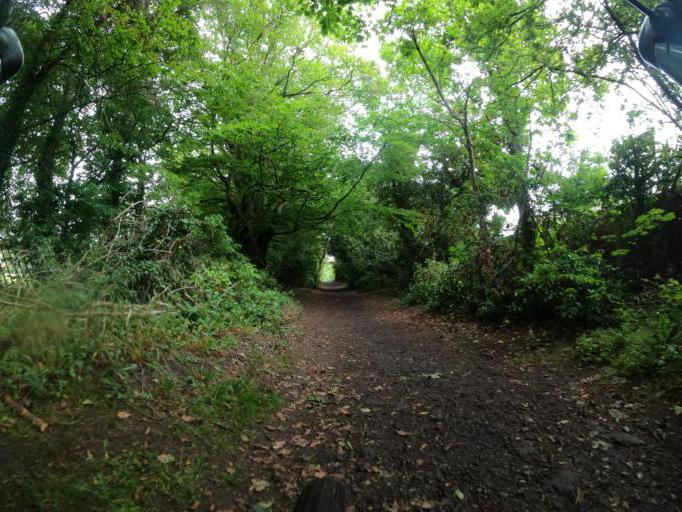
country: GB
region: Scotland
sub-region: Edinburgh
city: Currie
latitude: 55.9038
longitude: -3.3002
